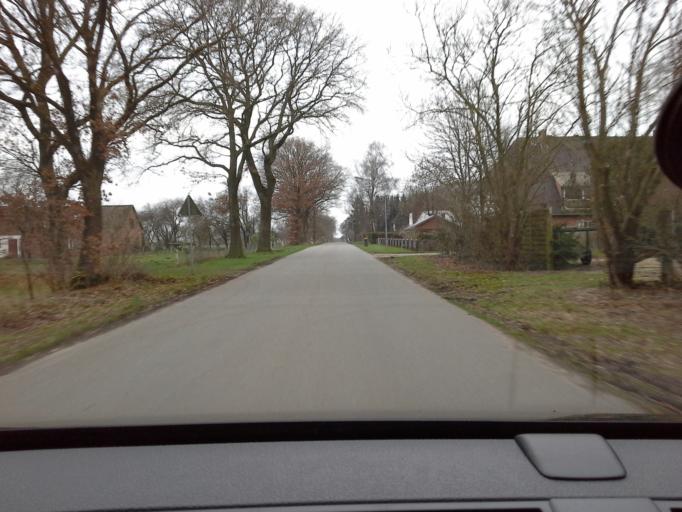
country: DE
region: Schleswig-Holstein
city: Lentfohrden
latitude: 53.8674
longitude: 9.8785
